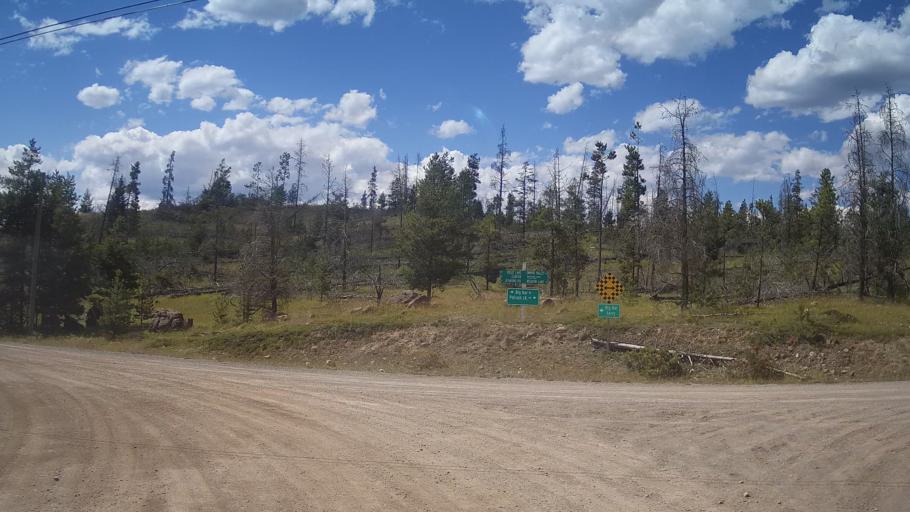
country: CA
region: British Columbia
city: Lillooet
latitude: 51.3358
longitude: -121.9709
